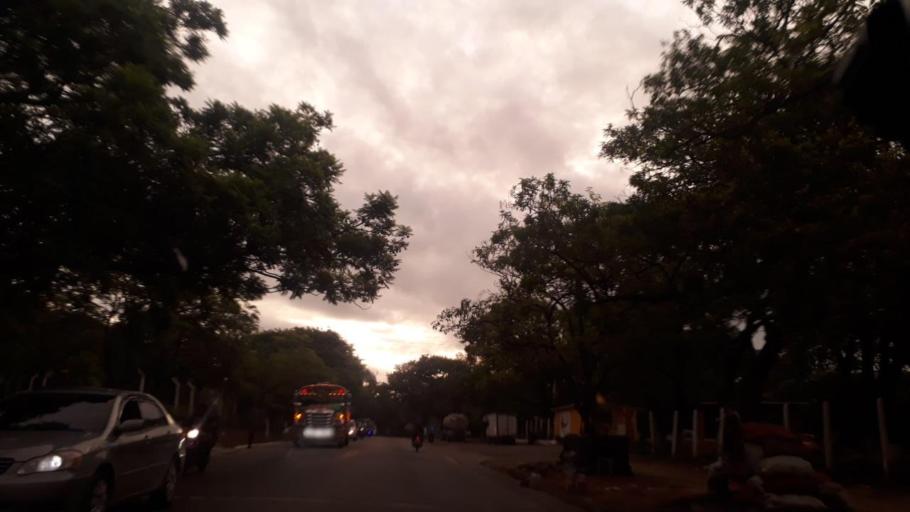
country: GT
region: Jutiapa
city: Jutiapa
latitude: 14.3006
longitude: -89.8935
